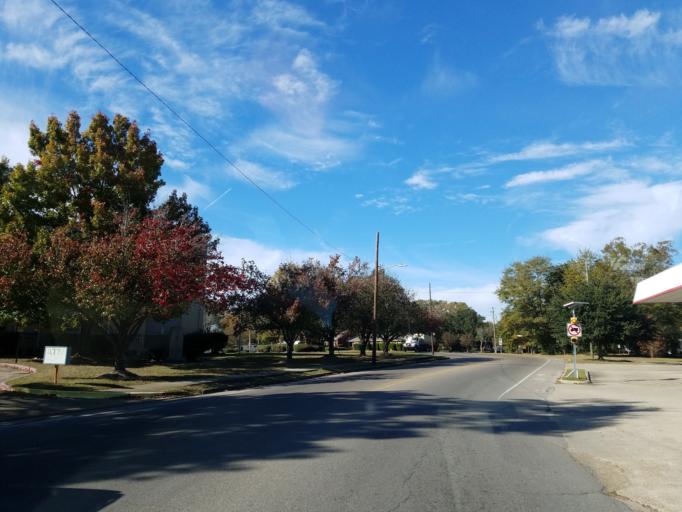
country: US
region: Mississippi
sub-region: Forrest County
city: Hattiesburg
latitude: 31.3168
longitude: -89.2856
